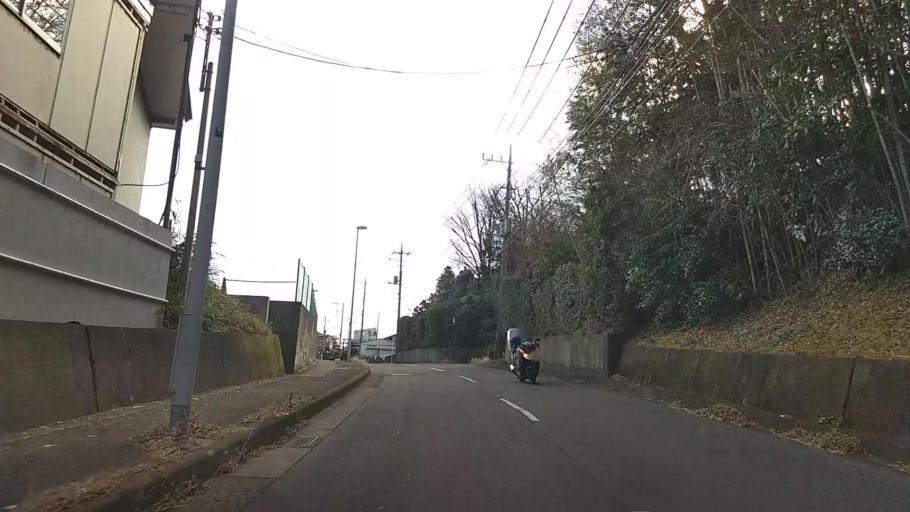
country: JP
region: Kanagawa
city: Atsugi
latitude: 35.4281
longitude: 139.3271
